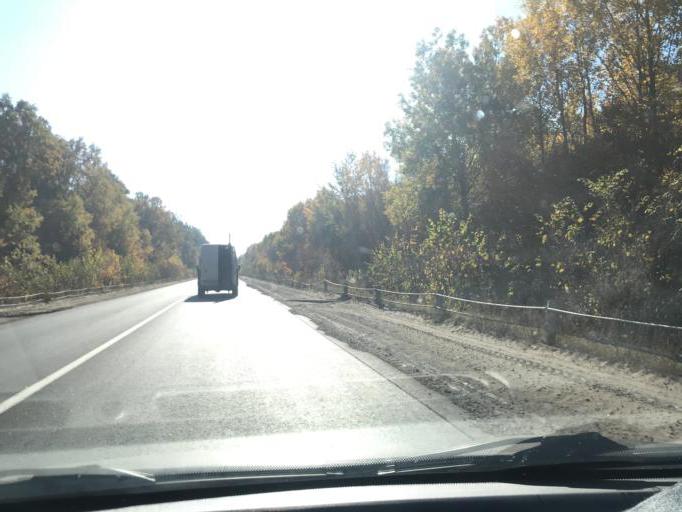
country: BY
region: Gomel
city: Gomel
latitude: 52.4145
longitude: 30.8286
